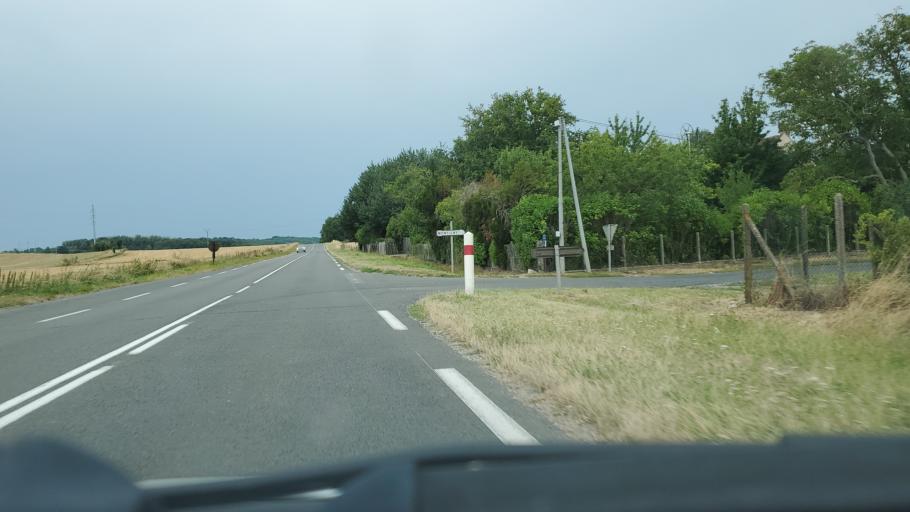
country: FR
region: Ile-de-France
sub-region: Departement de Seine-et-Marne
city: Chailly-en-Brie
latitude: 48.7943
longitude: 3.1076
